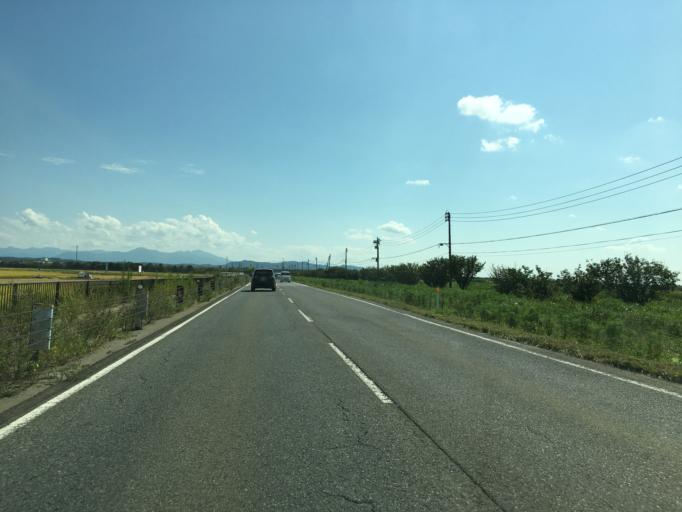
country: JP
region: Niigata
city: Niitsu-honcho
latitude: 37.8280
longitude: 139.0977
